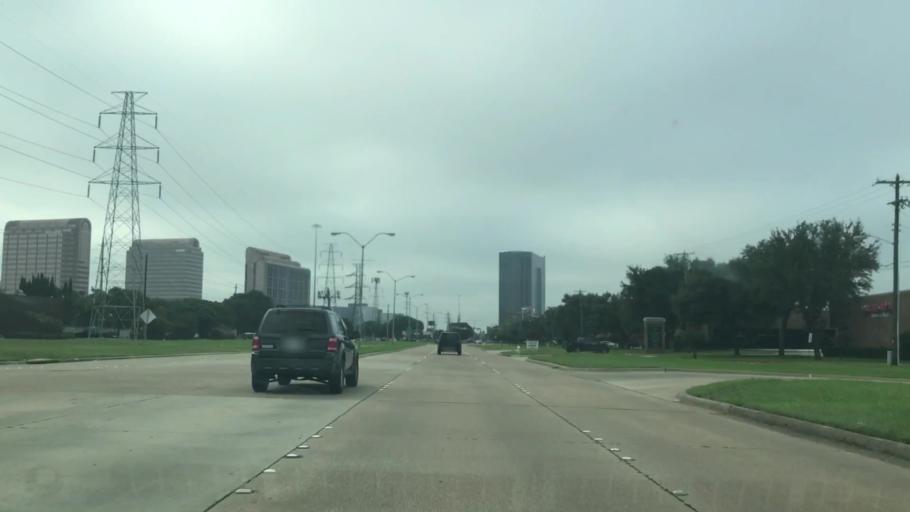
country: US
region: Texas
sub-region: Dallas County
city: Addison
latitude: 32.9361
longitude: -96.8240
